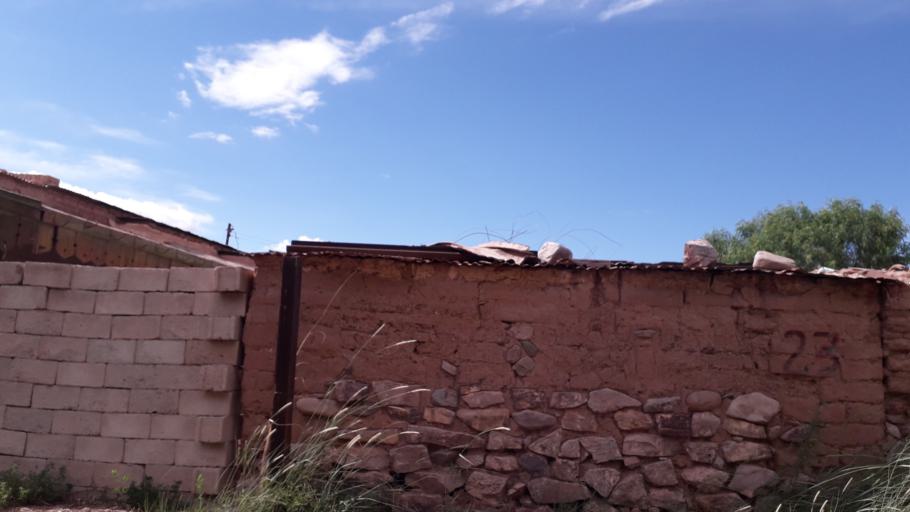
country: AR
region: Jujuy
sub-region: Departamento de Humahuaca
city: Humahuaca
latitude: -23.3076
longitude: -65.3530
